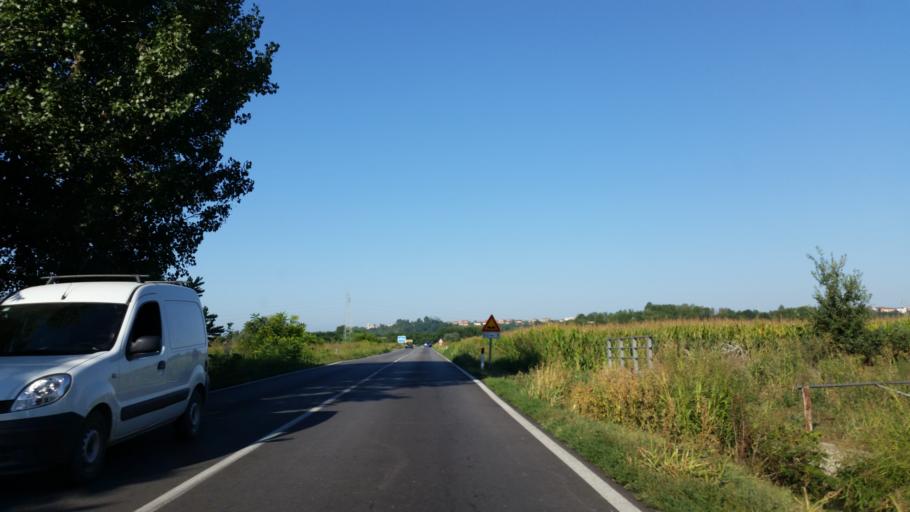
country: IT
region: Piedmont
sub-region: Provincia di Cuneo
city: Bra
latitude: 44.6766
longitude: 7.8708
